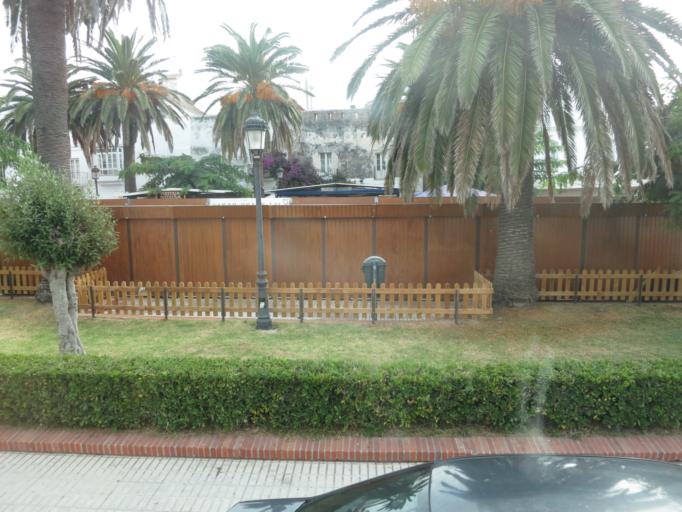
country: ES
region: Andalusia
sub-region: Provincia de Cadiz
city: Tarifa
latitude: 36.0121
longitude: -5.6048
